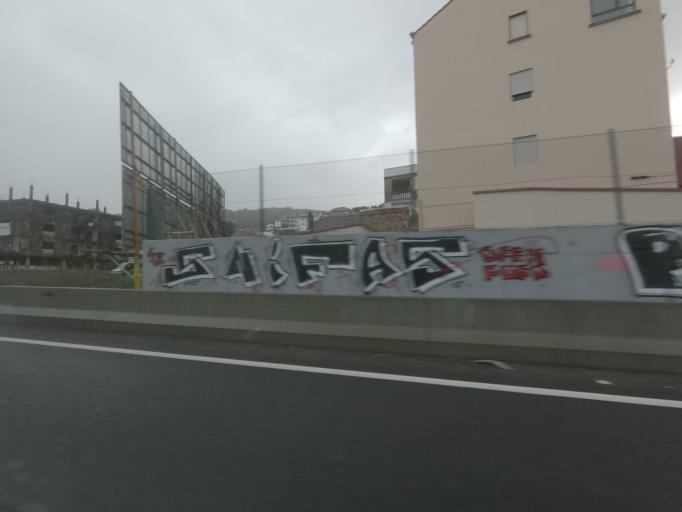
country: ES
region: Galicia
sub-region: Provincia de Pontevedra
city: Vigo
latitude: 42.2759
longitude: -8.6930
